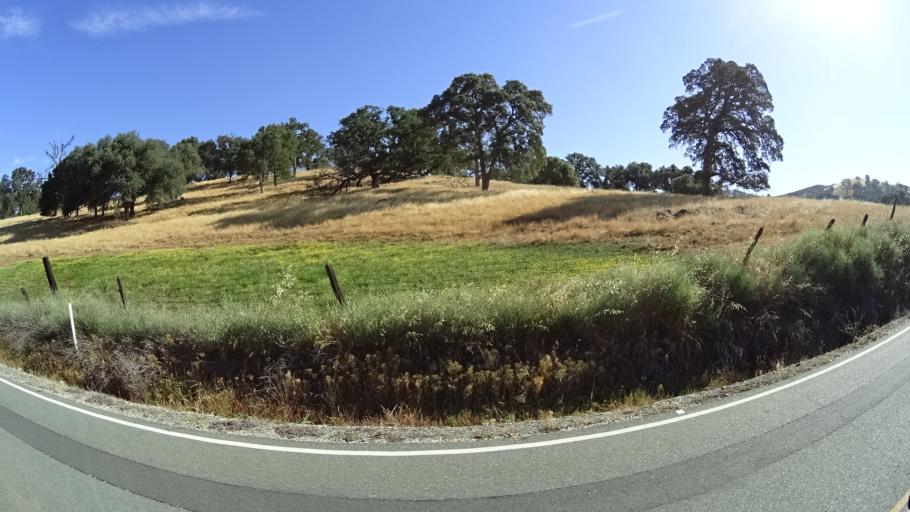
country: US
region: California
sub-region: Calaveras County
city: San Andreas
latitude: 38.1745
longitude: -120.6445
